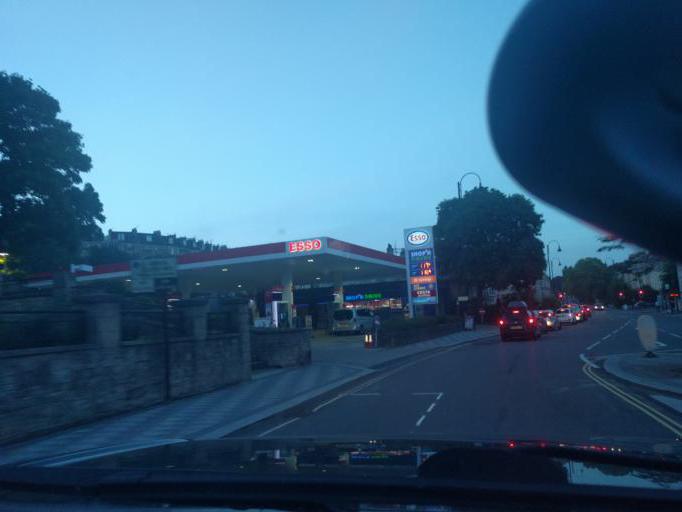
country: GB
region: England
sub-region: Bath and North East Somerset
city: Bath
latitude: 51.3918
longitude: -2.3531
